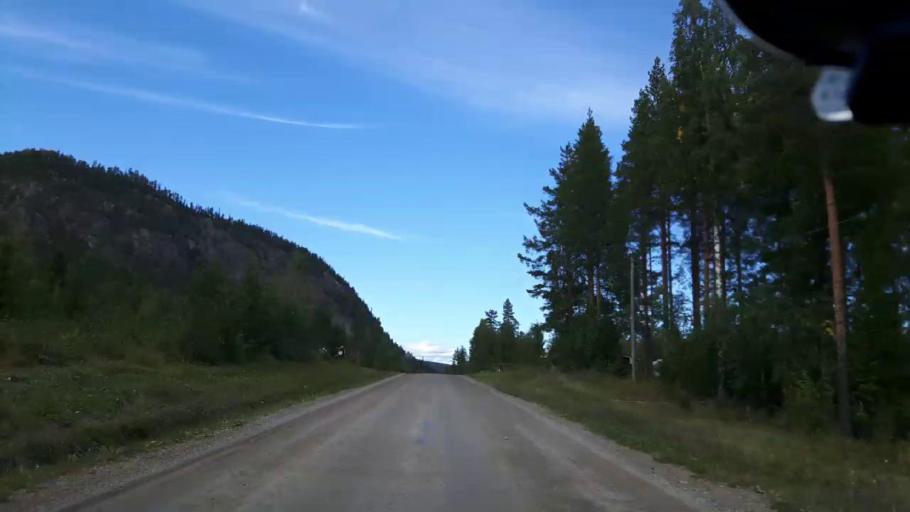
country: SE
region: Jaemtland
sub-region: Ragunda Kommun
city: Hammarstrand
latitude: 63.1287
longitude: 16.3242
